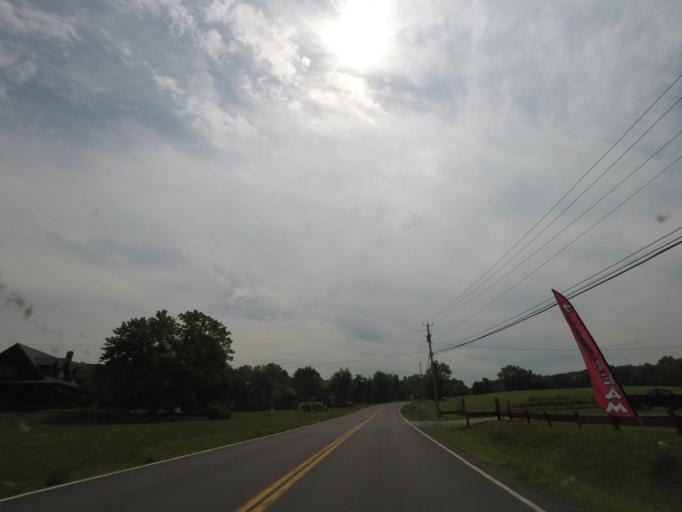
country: US
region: New York
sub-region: Saratoga County
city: Waterford
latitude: 42.7780
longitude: -73.6450
